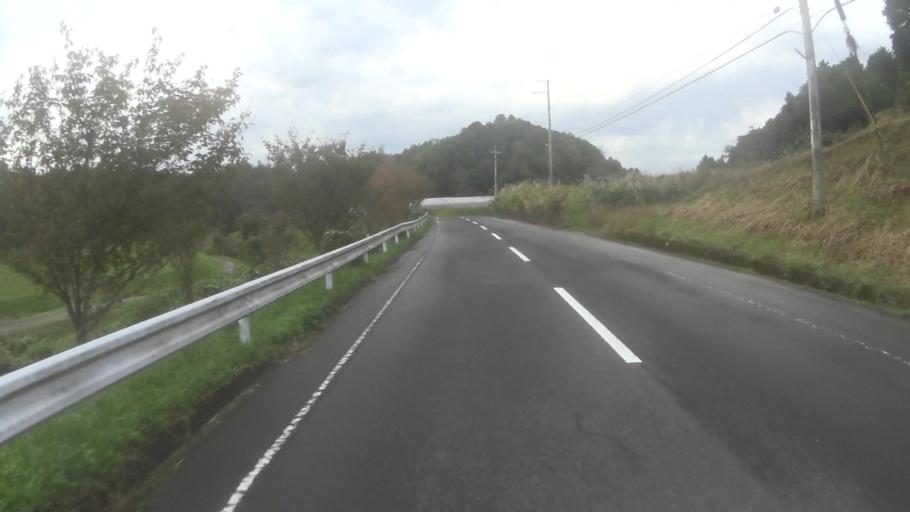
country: JP
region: Kyoto
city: Miyazu
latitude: 35.5060
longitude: 135.1283
